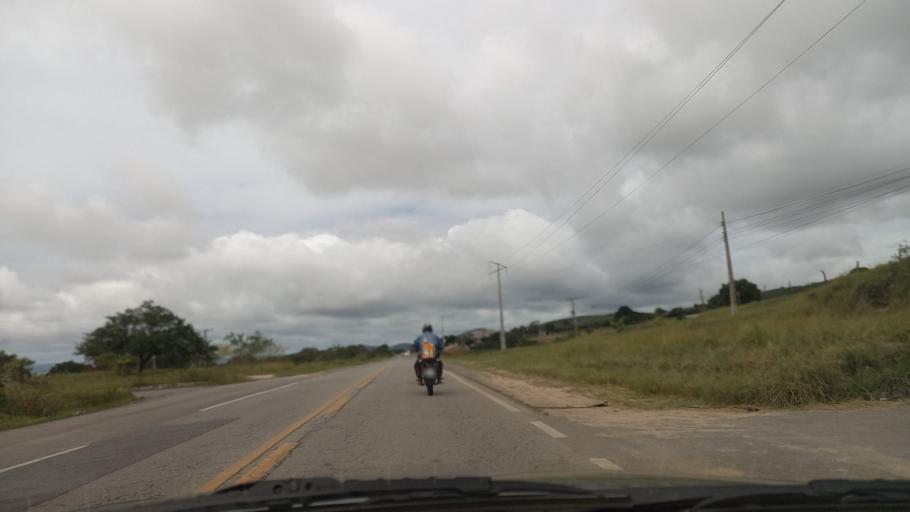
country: BR
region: Pernambuco
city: Garanhuns
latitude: -8.8790
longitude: -36.4370
